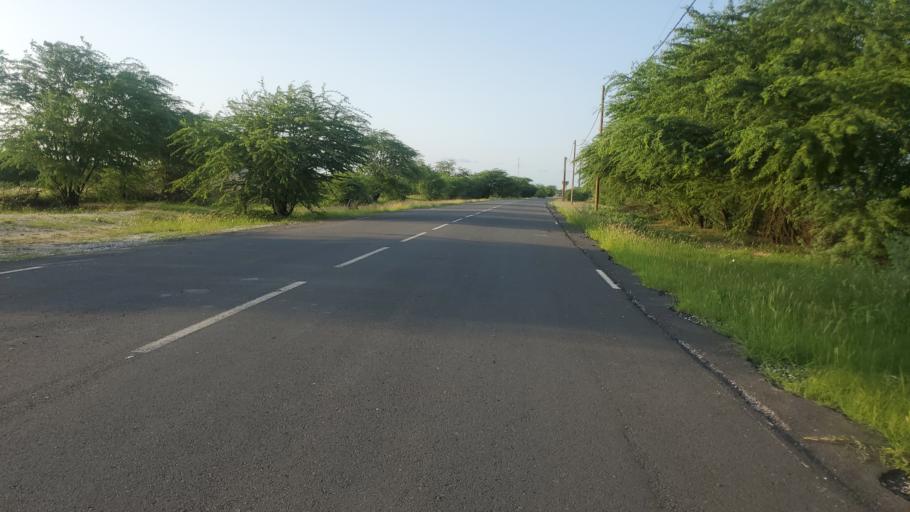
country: SN
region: Saint-Louis
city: Saint-Louis
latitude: 16.2083
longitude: -16.4155
